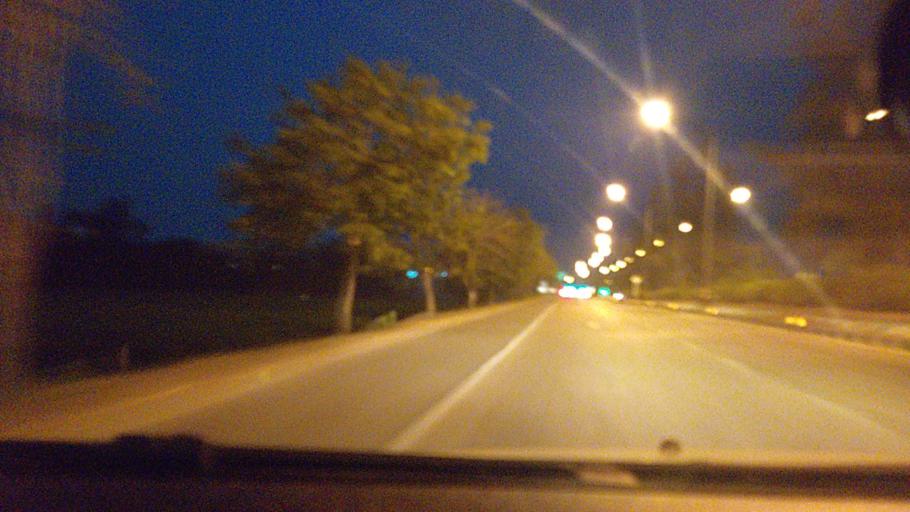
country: TH
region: Sing Buri
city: Sing Buri
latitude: 14.8737
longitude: 100.4288
